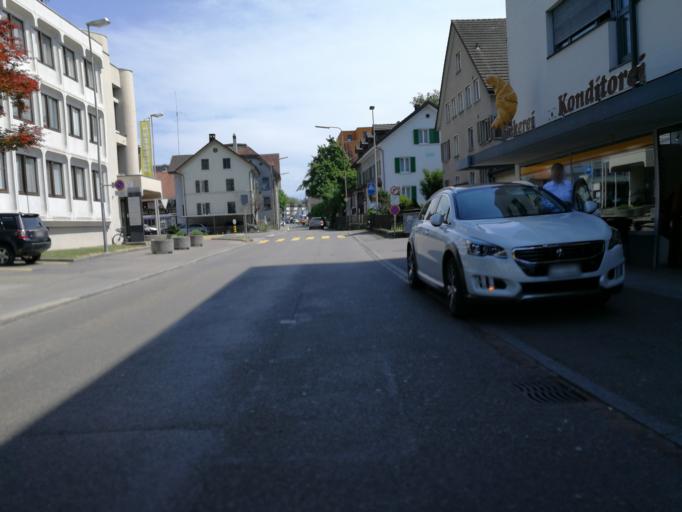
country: CH
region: Saint Gallen
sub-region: Wahlkreis See-Gaster
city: Rapperswil
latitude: 47.2294
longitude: 8.8287
